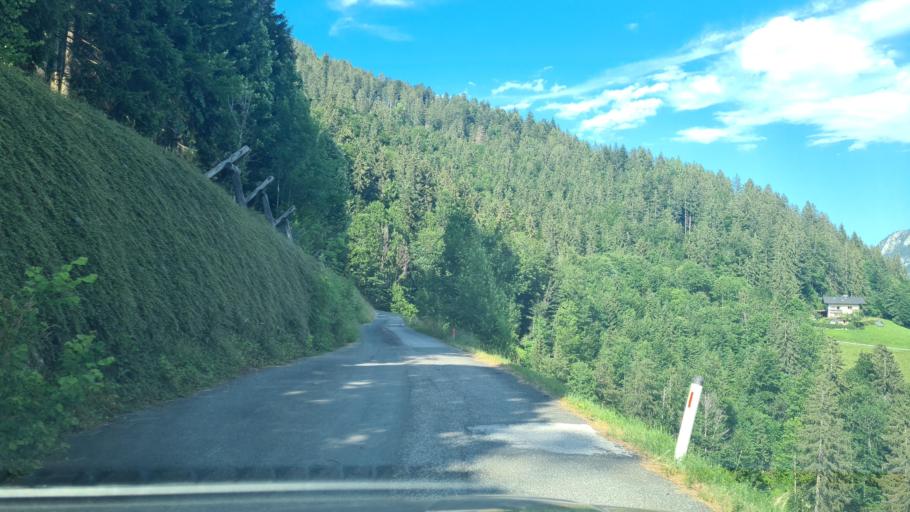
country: AT
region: Salzburg
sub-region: Politischer Bezirk Zell am See
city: Unken
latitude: 47.6503
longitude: 12.6986
